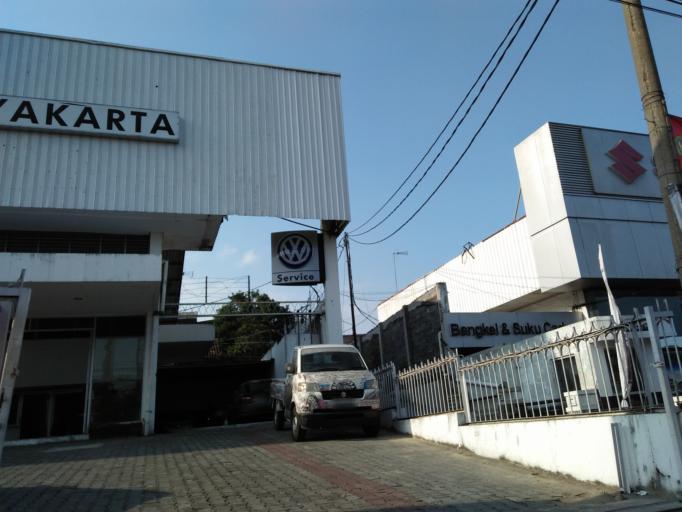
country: ID
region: Daerah Istimewa Yogyakarta
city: Depok
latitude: -7.7832
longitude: 110.4171
